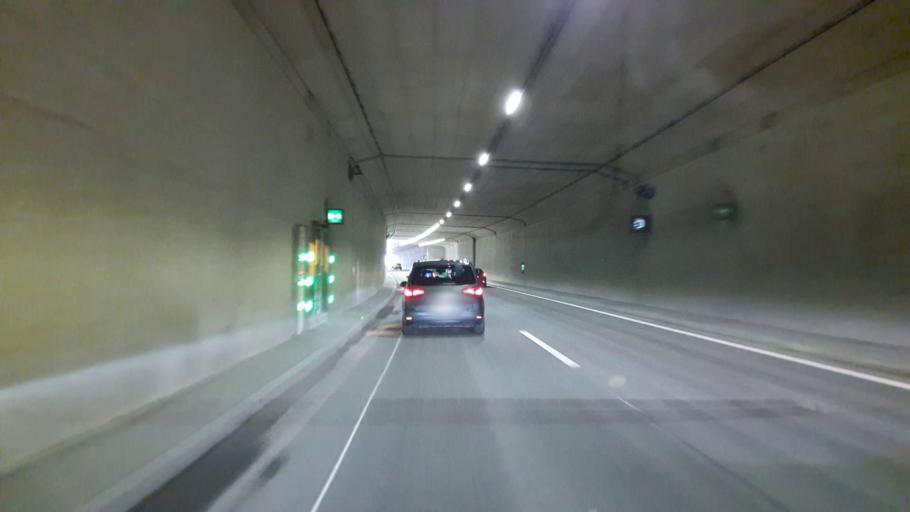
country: AT
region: Lower Austria
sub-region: Politischer Bezirk Wien-Umgebung
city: Gerasdorf bei Wien
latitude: 48.2329
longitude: 16.4544
